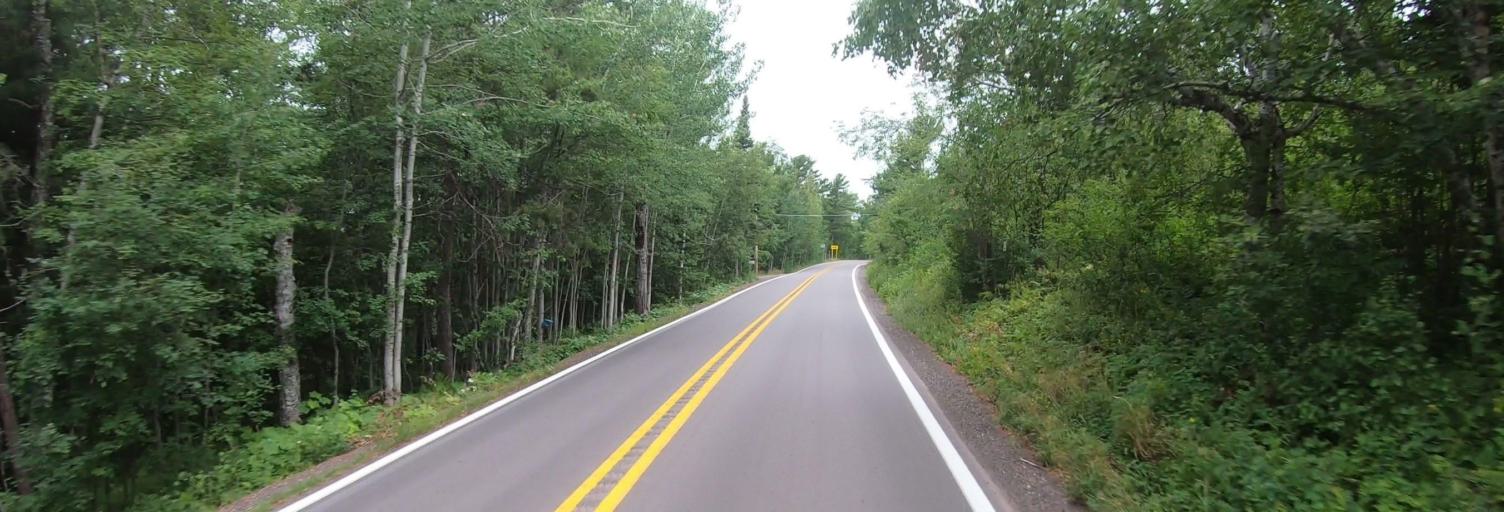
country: US
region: Michigan
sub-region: Keweenaw County
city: Eagle River
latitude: 47.4600
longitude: -88.1130
